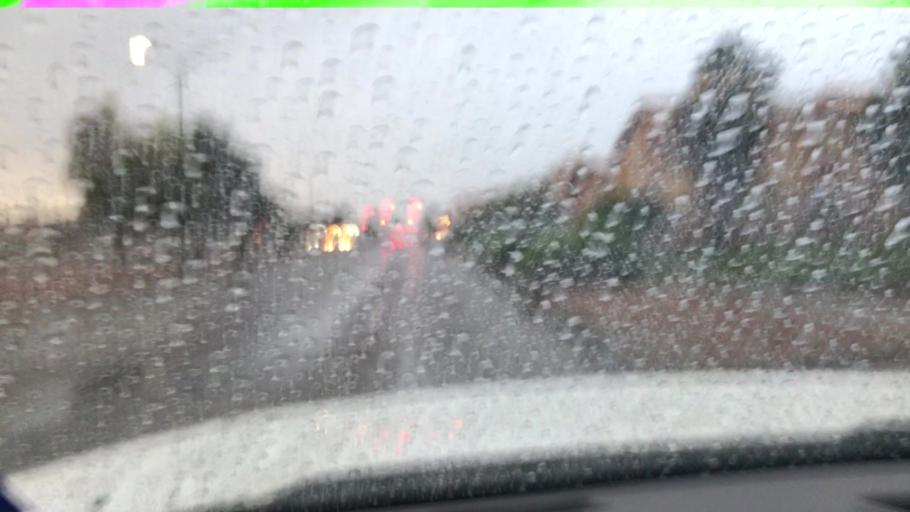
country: US
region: Texas
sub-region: El Paso County
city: Fort Bliss
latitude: 31.7932
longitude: -106.3234
